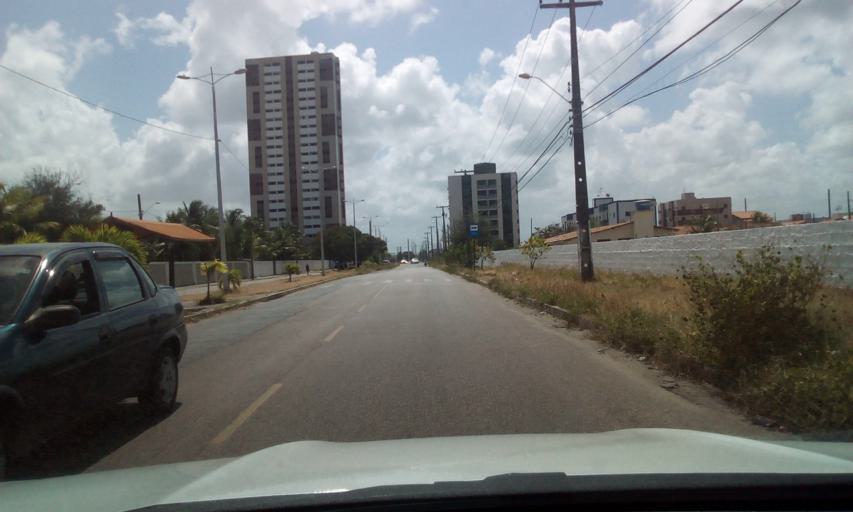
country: BR
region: Paraiba
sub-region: Joao Pessoa
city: Joao Pessoa
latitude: -7.0765
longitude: -34.8413
